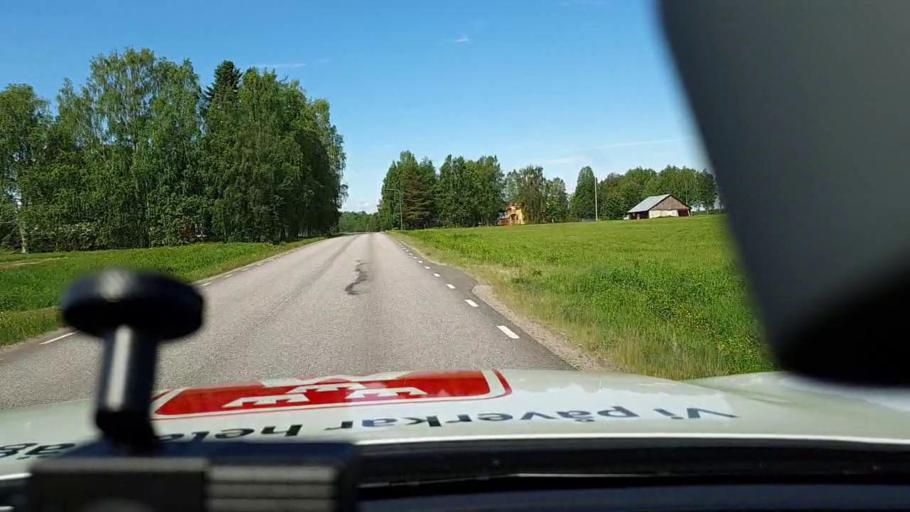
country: SE
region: Norrbotten
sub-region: Lulea Kommun
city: Sodra Sunderbyn
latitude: 65.6542
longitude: 21.8557
